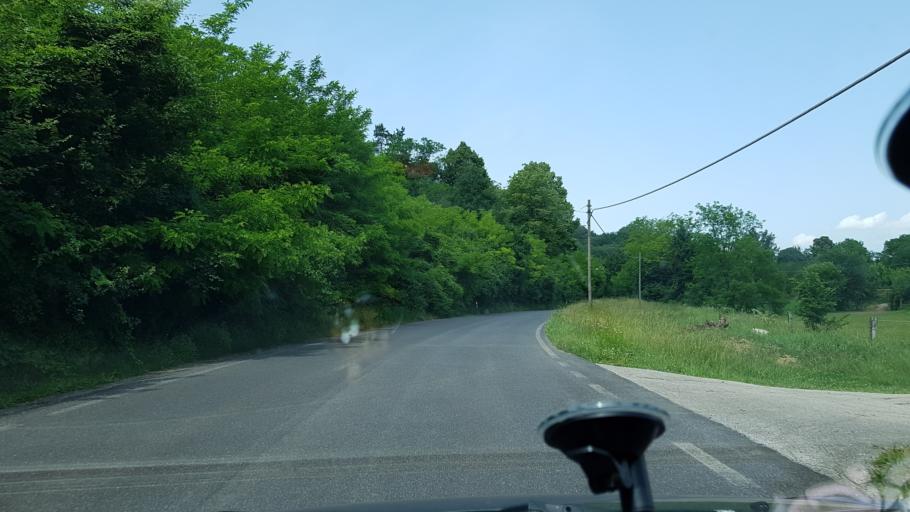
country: IT
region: Friuli Venezia Giulia
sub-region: Provincia di Gorizia
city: Savogna d'Isonzo
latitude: 45.8908
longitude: 13.5757
